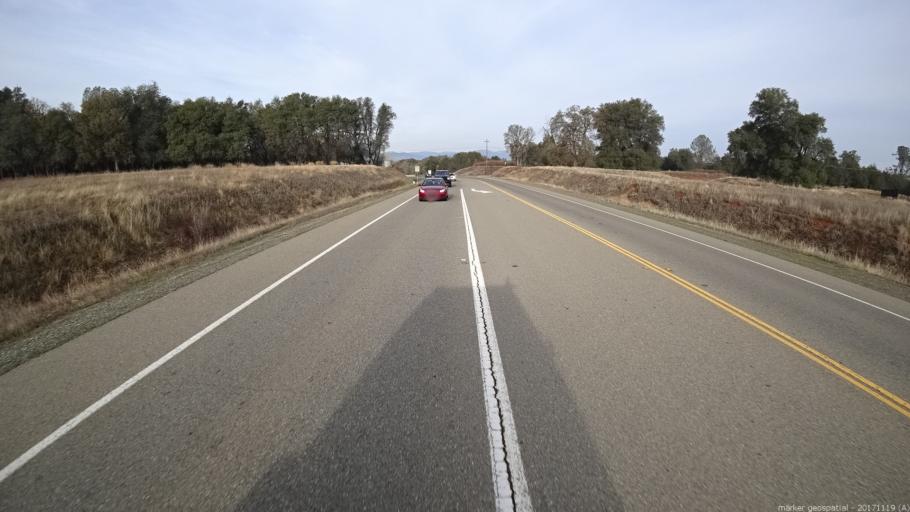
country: US
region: California
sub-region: Shasta County
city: Anderson
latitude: 40.5077
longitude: -122.3136
